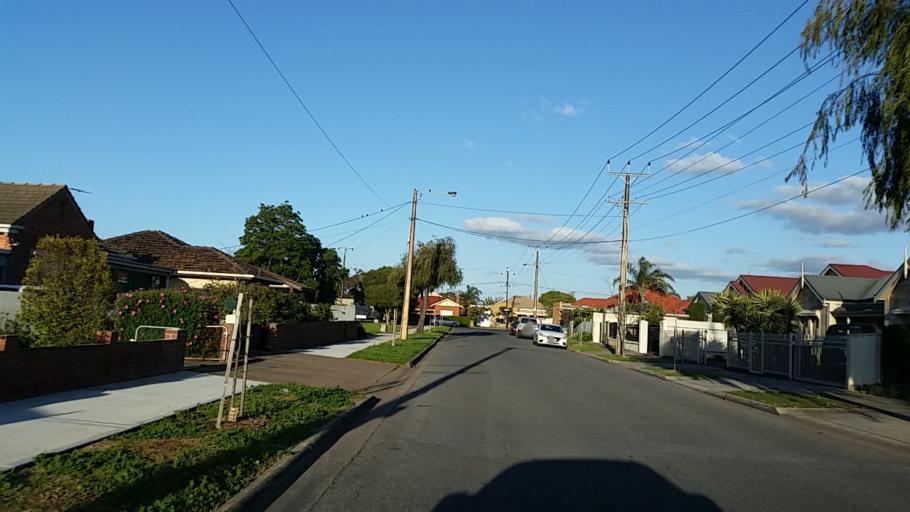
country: AU
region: South Australia
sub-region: Charles Sturt
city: Findon
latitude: -34.8921
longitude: 138.5399
